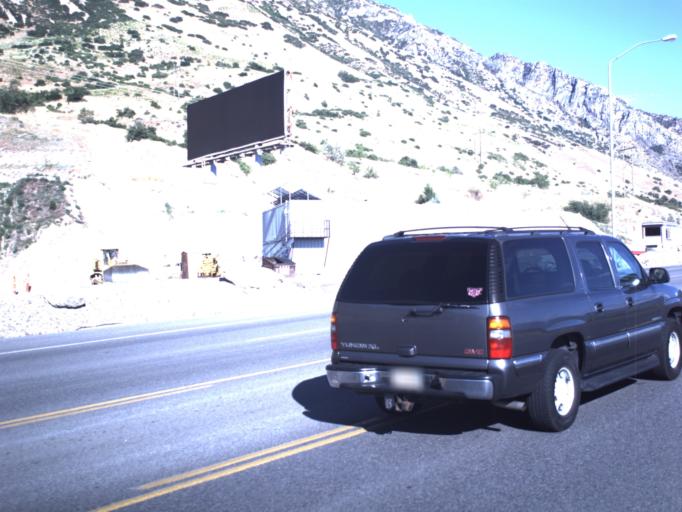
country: US
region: Utah
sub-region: Utah County
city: Springville
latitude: 40.1960
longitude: -111.6161
